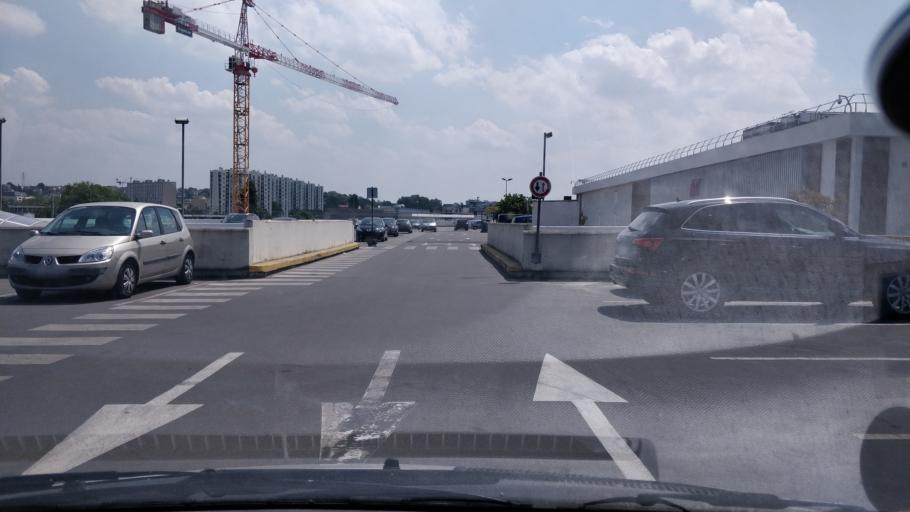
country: FR
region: Ile-de-France
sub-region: Departement de Seine-Saint-Denis
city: Noisy-le-Sec
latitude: 48.8839
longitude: 2.4788
